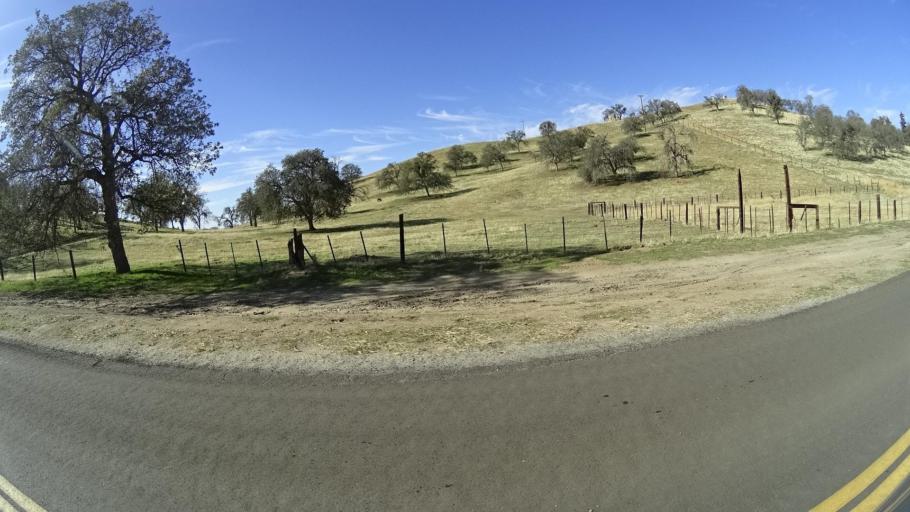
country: US
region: California
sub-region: Kern County
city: Oildale
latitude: 35.6493
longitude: -118.8407
